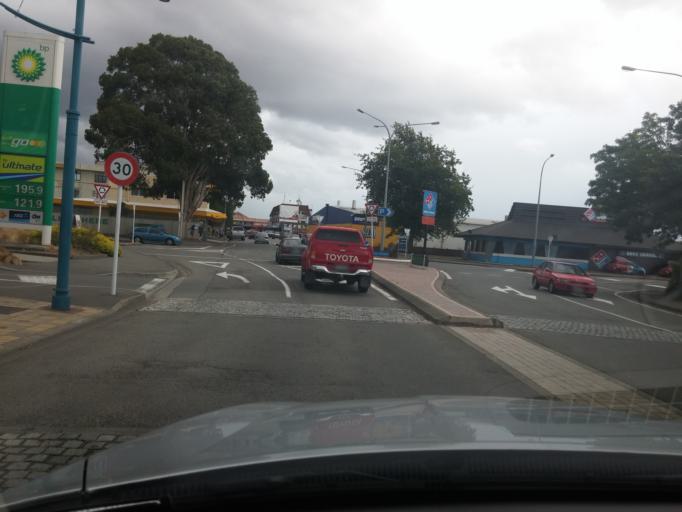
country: NZ
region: Marlborough
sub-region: Marlborough District
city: Blenheim
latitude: -41.5136
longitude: 173.9594
